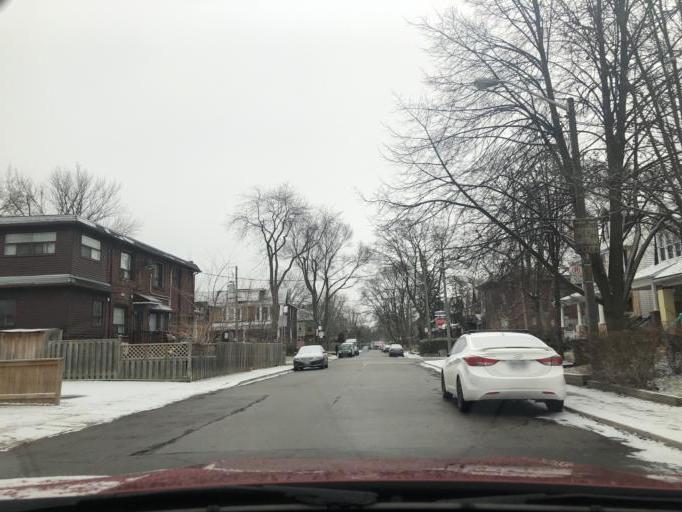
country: CA
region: Ontario
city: Toronto
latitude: 43.6838
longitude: -79.3408
